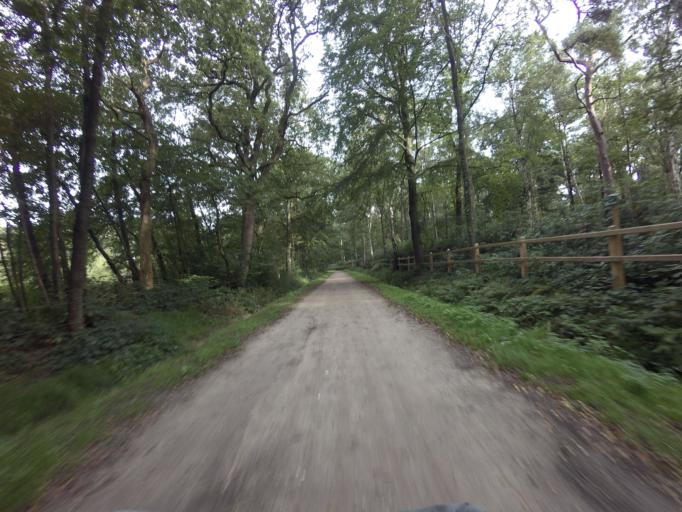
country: NL
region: Overijssel
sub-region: Gemeente Enschede
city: Enschede
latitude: 52.1936
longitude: 6.9131
